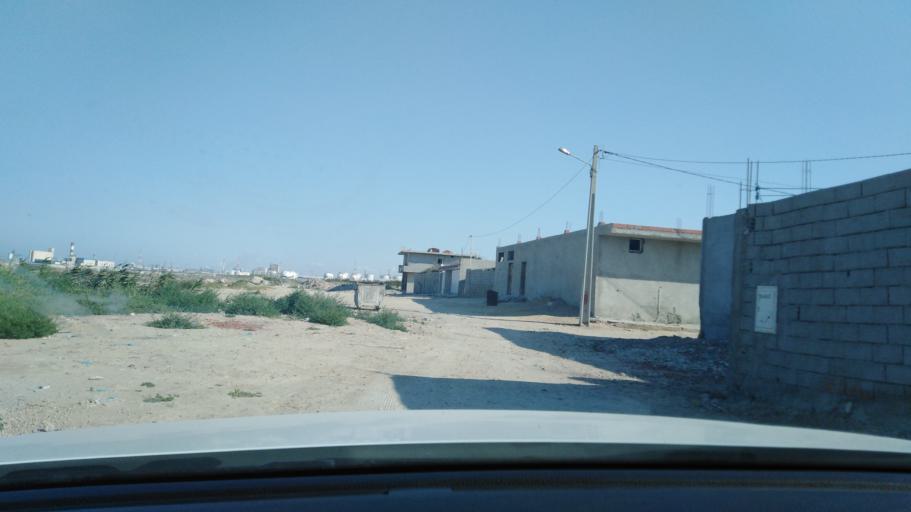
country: TN
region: Qabis
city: Gabes
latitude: 33.9418
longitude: 10.0779
